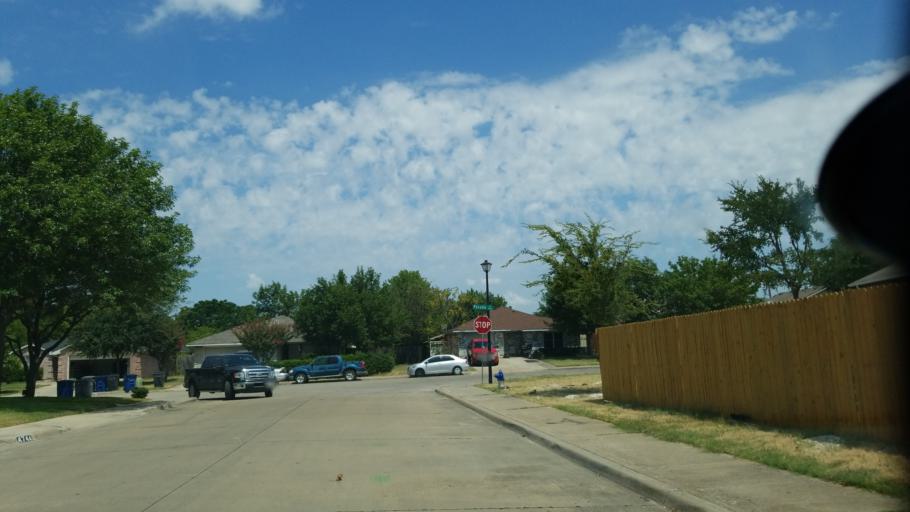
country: US
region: Texas
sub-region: Dallas County
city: Cockrell Hill
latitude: 32.7292
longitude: -96.8976
